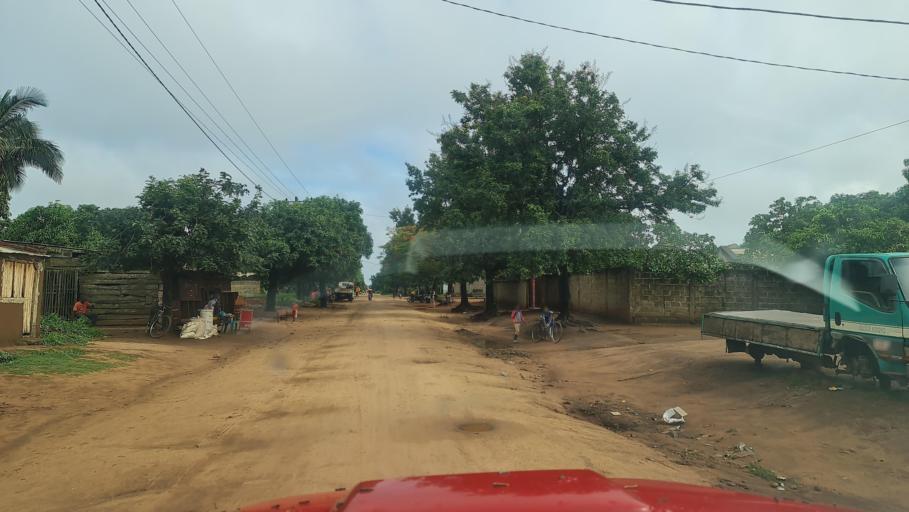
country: MW
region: Southern Region
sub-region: Nsanje District
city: Nsanje
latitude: -17.3224
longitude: 35.5917
